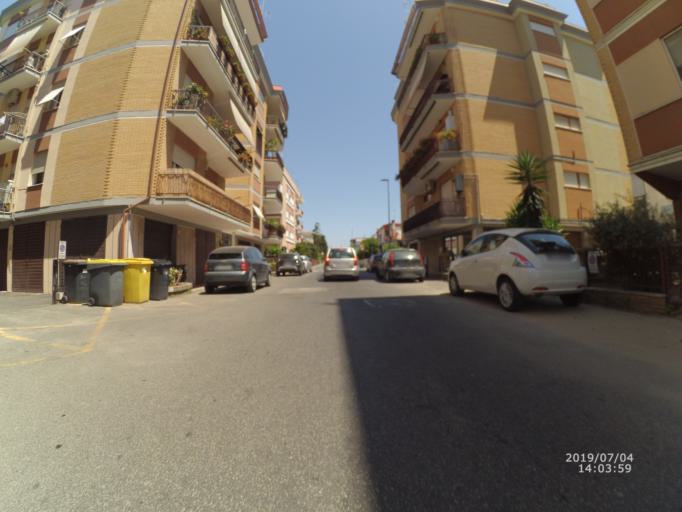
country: IT
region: Latium
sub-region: Provincia di Latina
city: Terracina
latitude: 41.2860
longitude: 13.2432
